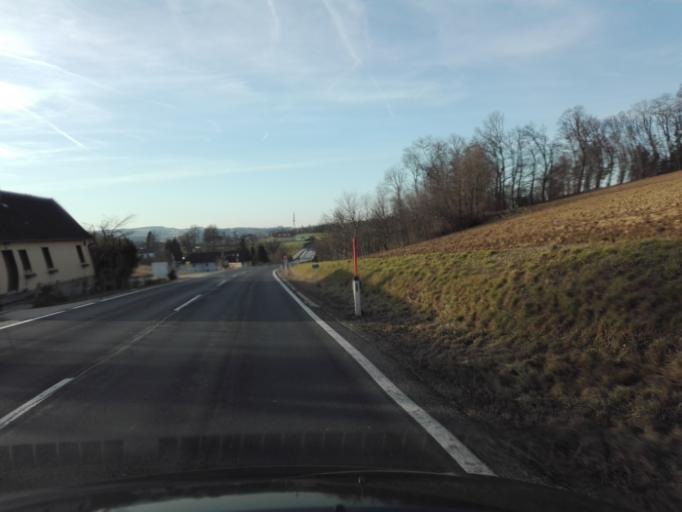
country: AT
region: Lower Austria
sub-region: Politischer Bezirk Amstetten
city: Strengberg
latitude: 48.1476
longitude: 14.6310
